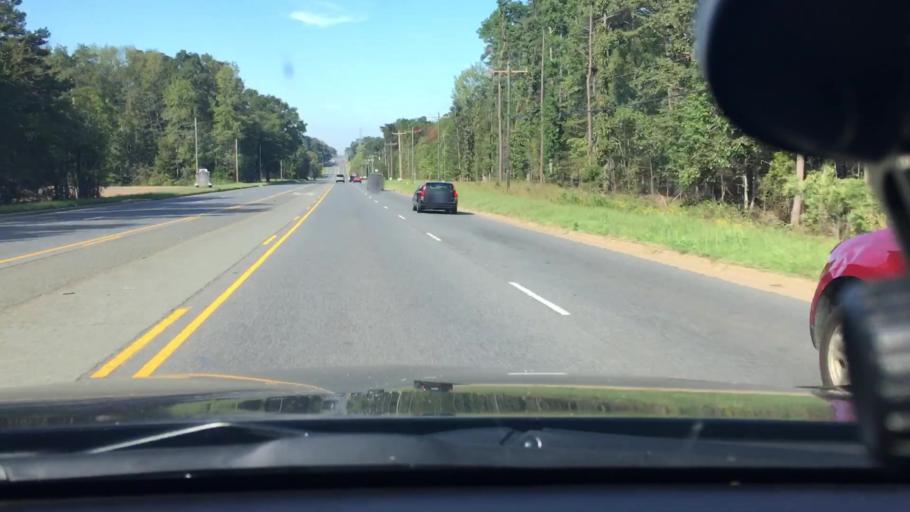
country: US
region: North Carolina
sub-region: Cabarrus County
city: Midland
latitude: 35.2500
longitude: -80.5151
